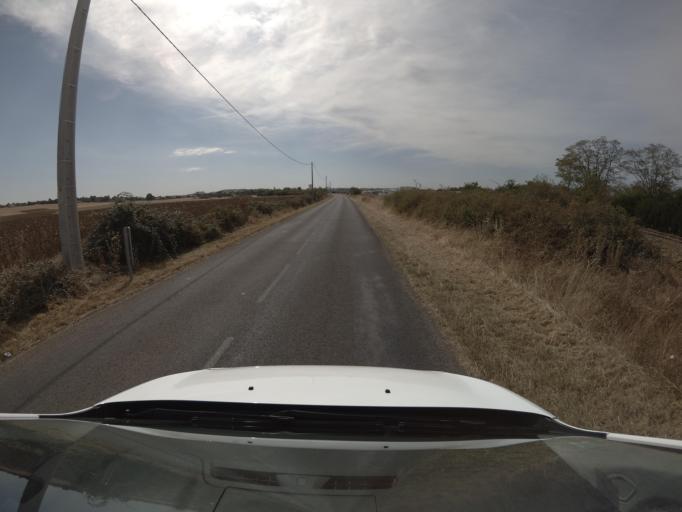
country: FR
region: Poitou-Charentes
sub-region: Departement des Deux-Sevres
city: Thouars
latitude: 46.9819
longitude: -0.1867
